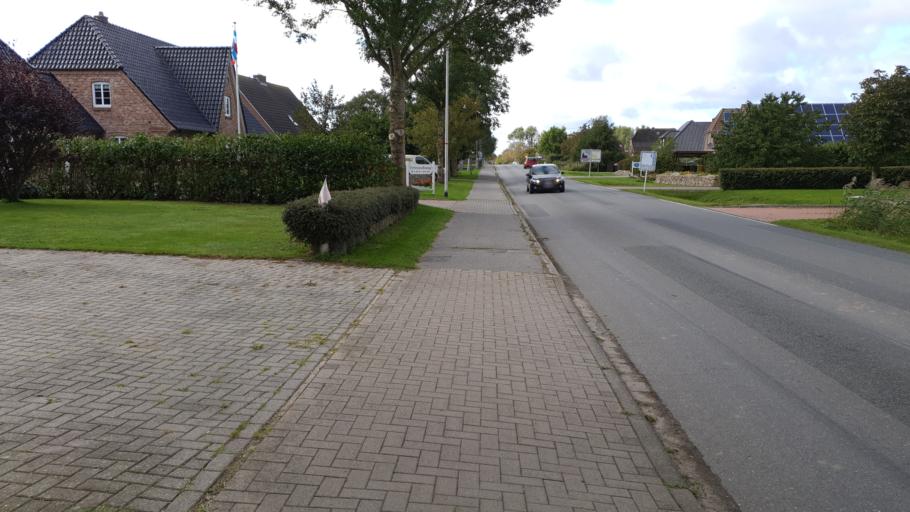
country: DE
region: Schleswig-Holstein
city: Elisabeth-Sophien-Koog
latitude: 54.4894
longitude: 8.8780
